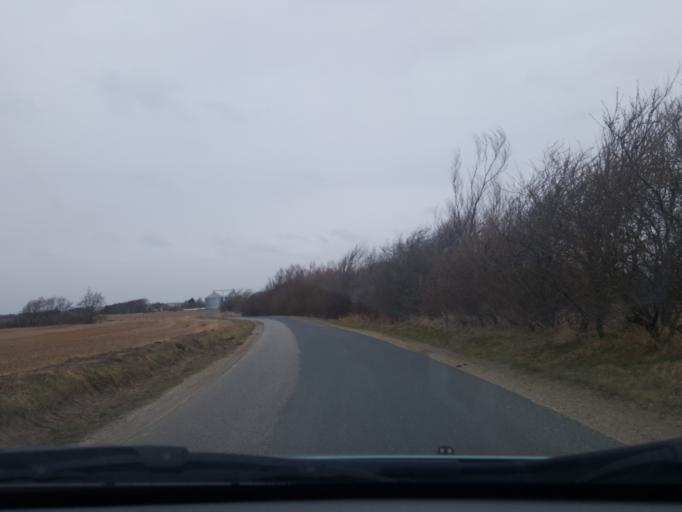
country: DK
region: Central Jutland
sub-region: Holstebro Kommune
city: Ulfborg
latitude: 56.2259
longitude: 8.2709
